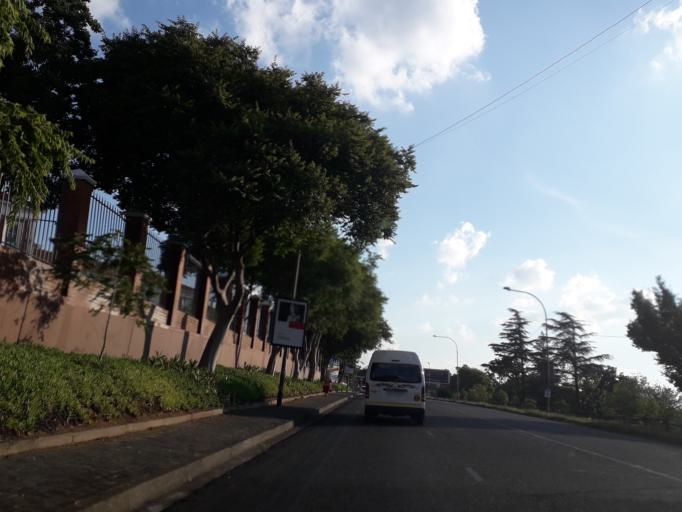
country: ZA
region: Gauteng
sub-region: City of Johannesburg Metropolitan Municipality
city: Johannesburg
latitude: -26.1415
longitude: 28.0089
